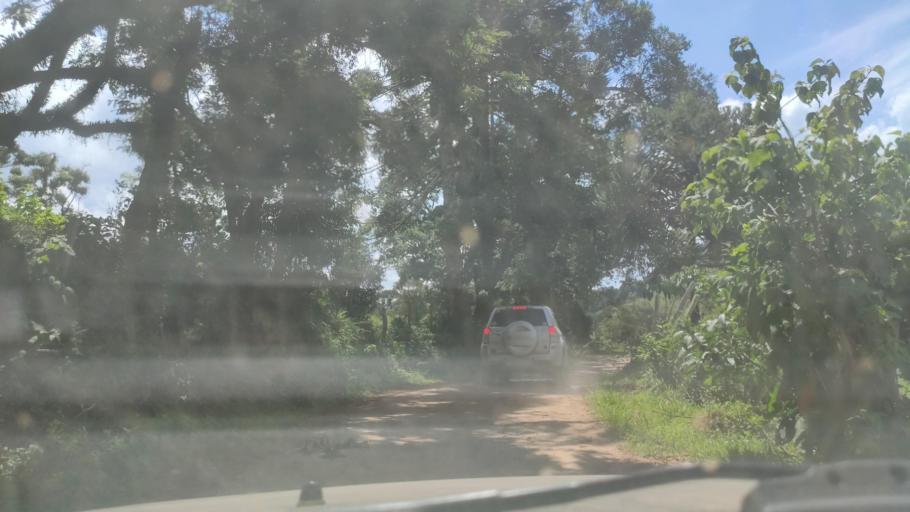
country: BR
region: Minas Gerais
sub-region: Cambui
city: Cambui
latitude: -22.6988
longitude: -45.9949
